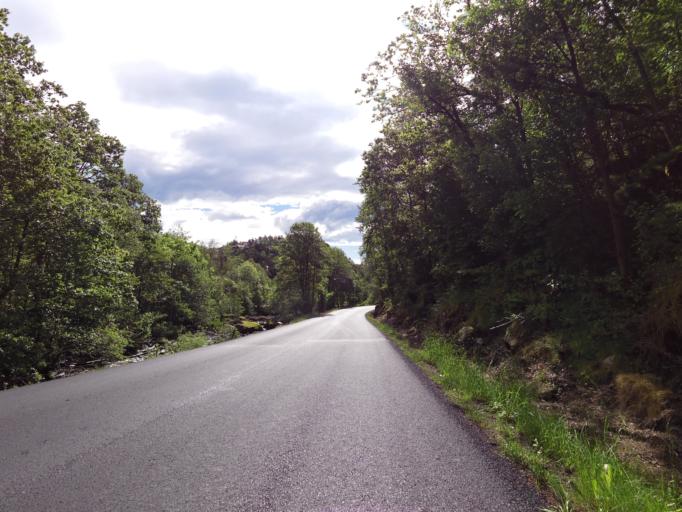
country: NO
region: Vest-Agder
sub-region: Lindesnes
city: Vigeland
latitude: 58.0540
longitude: 7.2384
